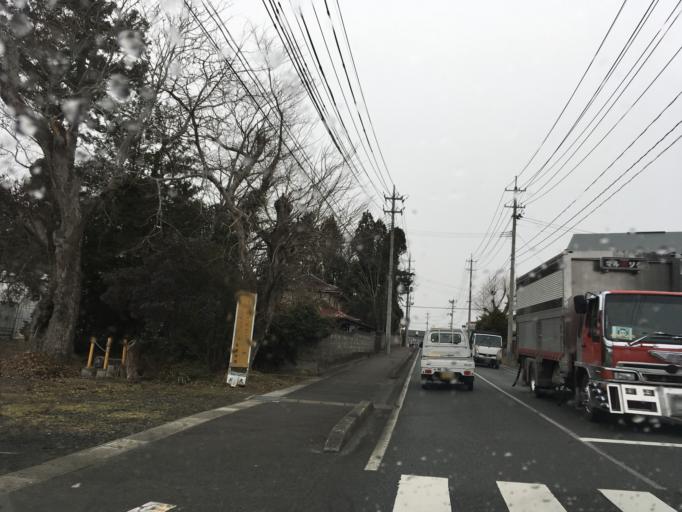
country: JP
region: Iwate
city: Ichinoseki
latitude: 38.8350
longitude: 141.1774
